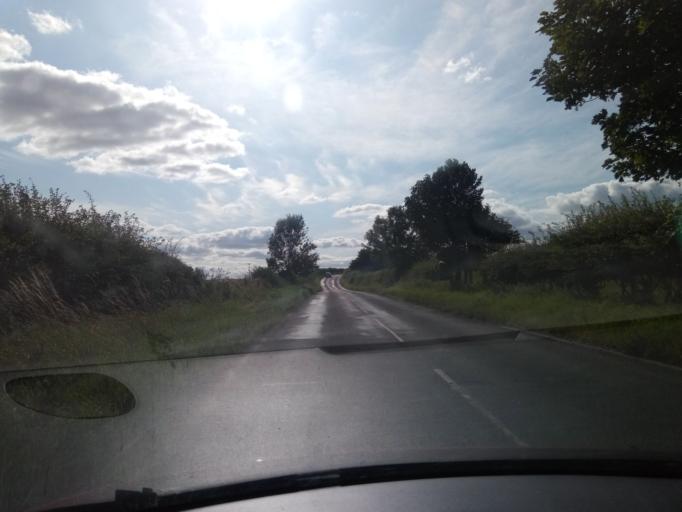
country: GB
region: England
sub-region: Northumberland
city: Berwick-Upon-Tweed
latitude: 55.7659
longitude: -2.0733
